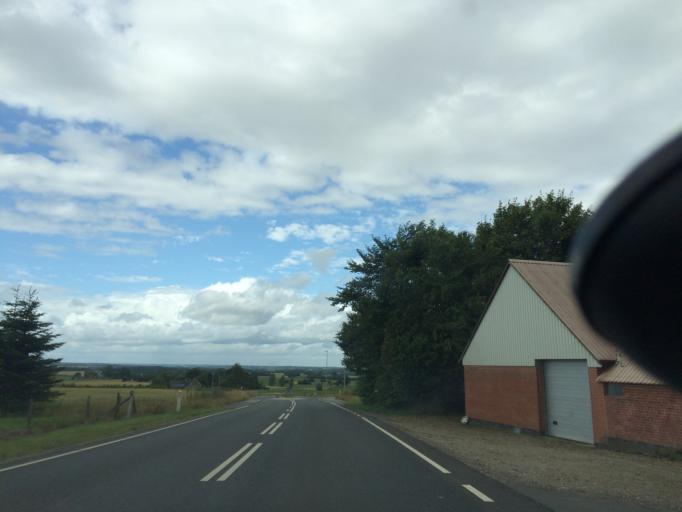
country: DK
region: Central Jutland
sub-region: Skanderborg Kommune
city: Ry
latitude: 56.1791
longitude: 9.7658
